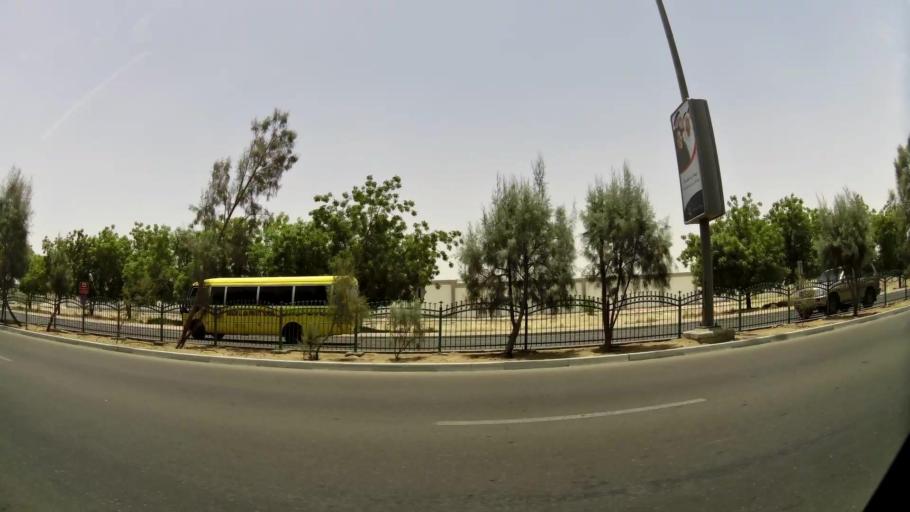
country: AE
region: Abu Dhabi
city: Al Ain
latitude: 24.2053
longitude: 55.7516
